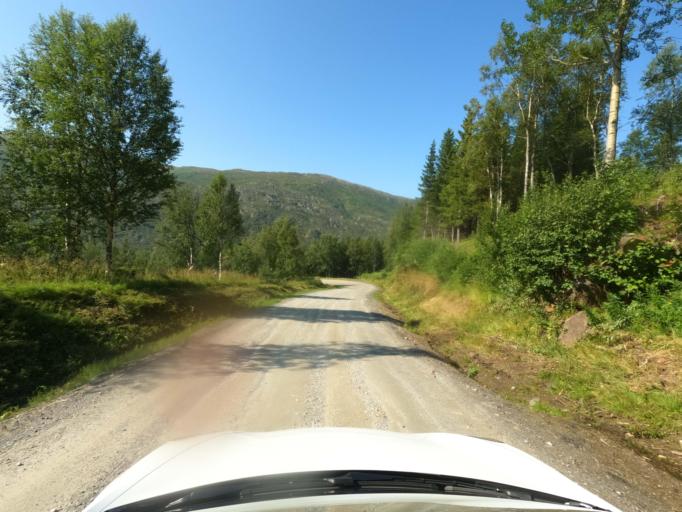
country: NO
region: Nordland
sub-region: Ballangen
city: Ballangen
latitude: 68.2624
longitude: 16.7147
